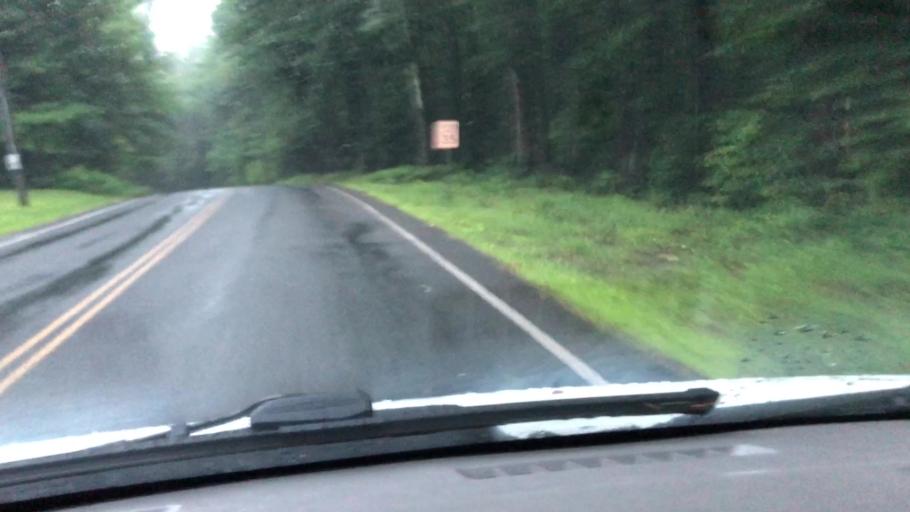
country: US
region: Massachusetts
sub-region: Hampshire County
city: Westhampton
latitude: 42.2774
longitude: -72.7521
